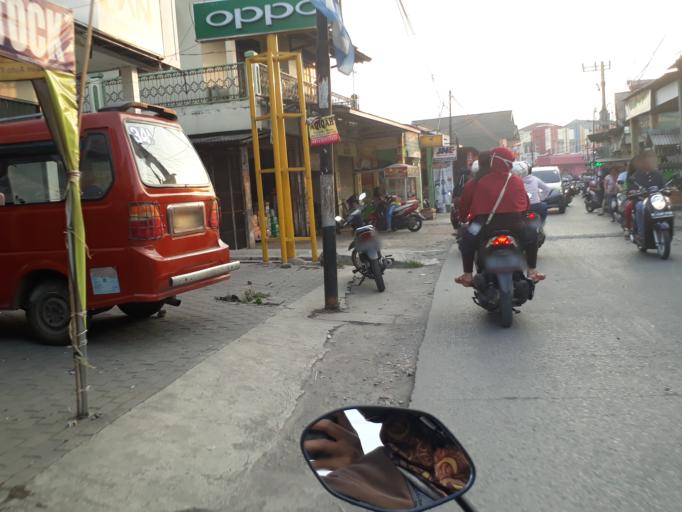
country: ID
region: West Java
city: Bekasi
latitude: -6.2435
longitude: 107.0464
